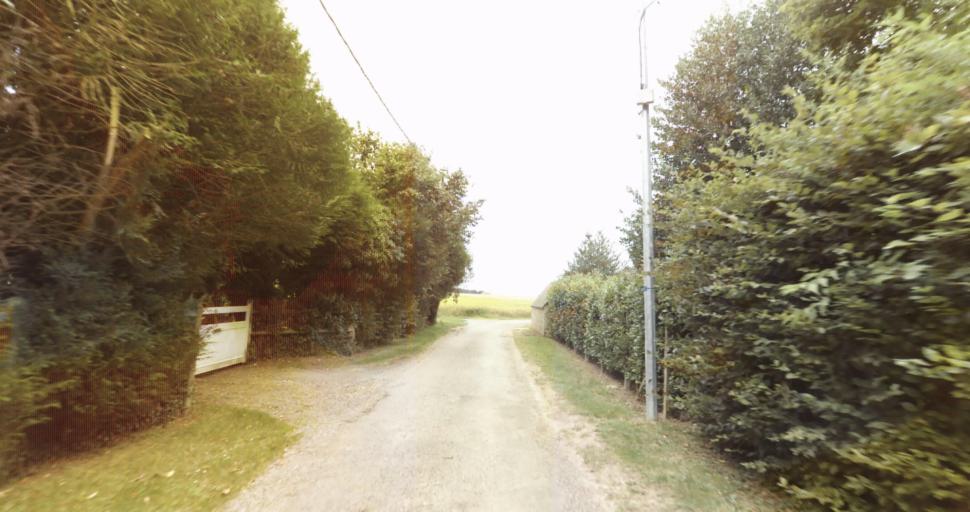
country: FR
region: Haute-Normandie
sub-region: Departement de l'Eure
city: La Couture-Boussey
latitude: 48.9286
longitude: 1.3385
